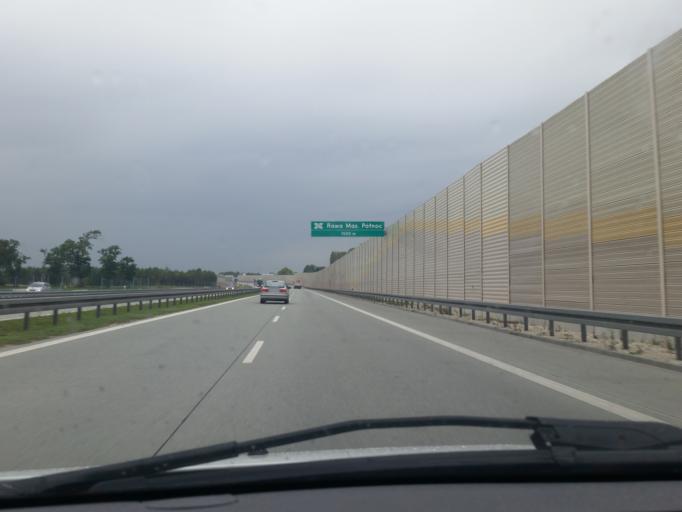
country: PL
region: Lodz Voivodeship
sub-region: Powiat rawski
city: Rawa Mazowiecka
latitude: 51.7876
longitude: 20.2834
